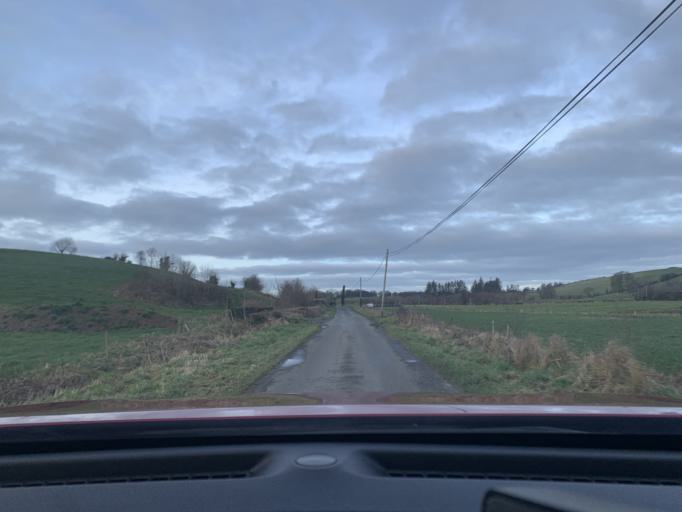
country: IE
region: Connaught
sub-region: Sligo
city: Ballymote
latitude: 54.0582
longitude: -8.5652
